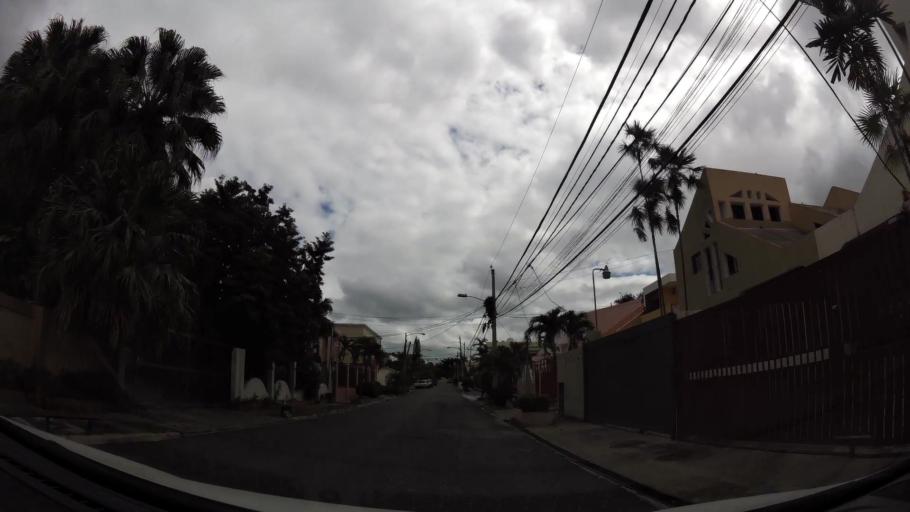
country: DO
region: Nacional
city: Bella Vista
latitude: 18.4713
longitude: -69.9554
